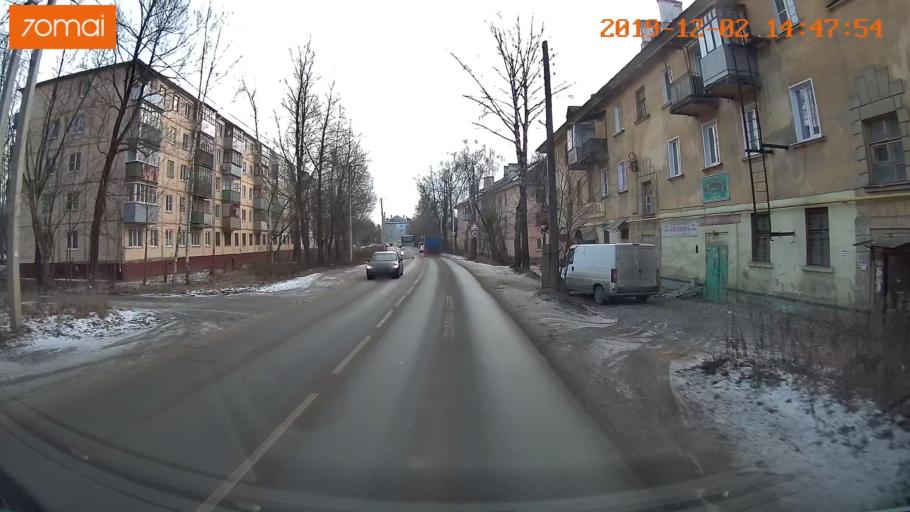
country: RU
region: Ivanovo
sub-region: Gorod Ivanovo
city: Ivanovo
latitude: 56.9865
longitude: 41.0174
